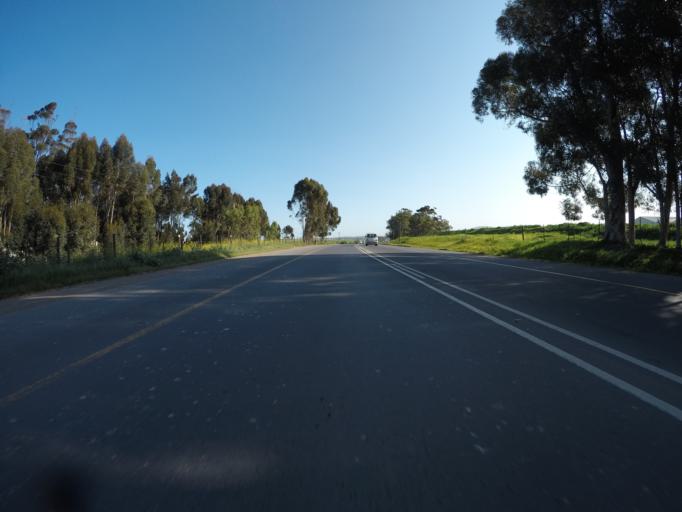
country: ZA
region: Western Cape
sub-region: City of Cape Town
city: Kraaifontein
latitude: -33.7950
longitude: 18.6936
